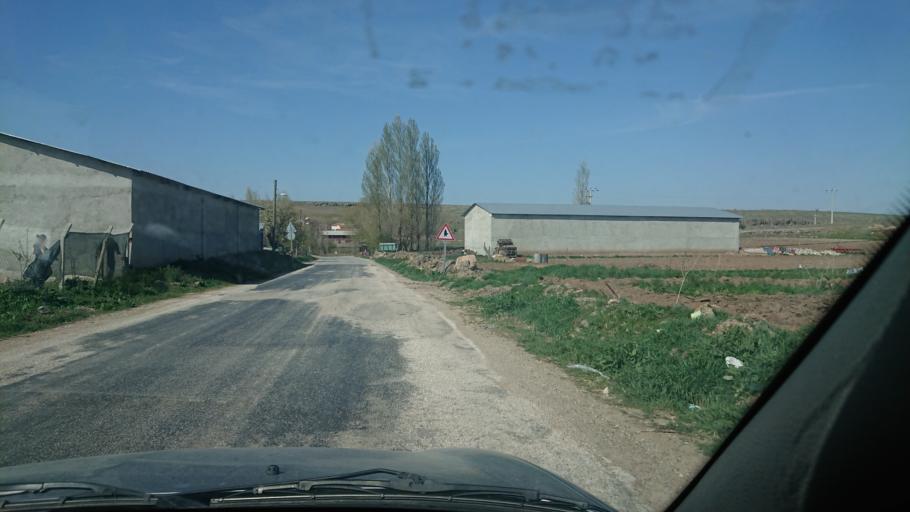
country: TR
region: Eskisehir
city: Eskisehir
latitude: 39.6768
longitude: 30.4849
